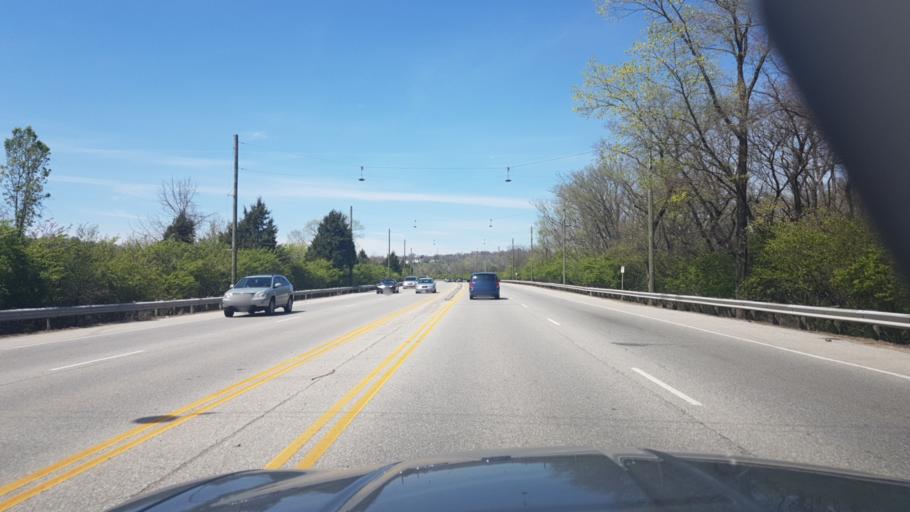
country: US
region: Ohio
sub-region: Hamilton County
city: Turpin Hills
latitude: 39.1111
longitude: -84.4030
